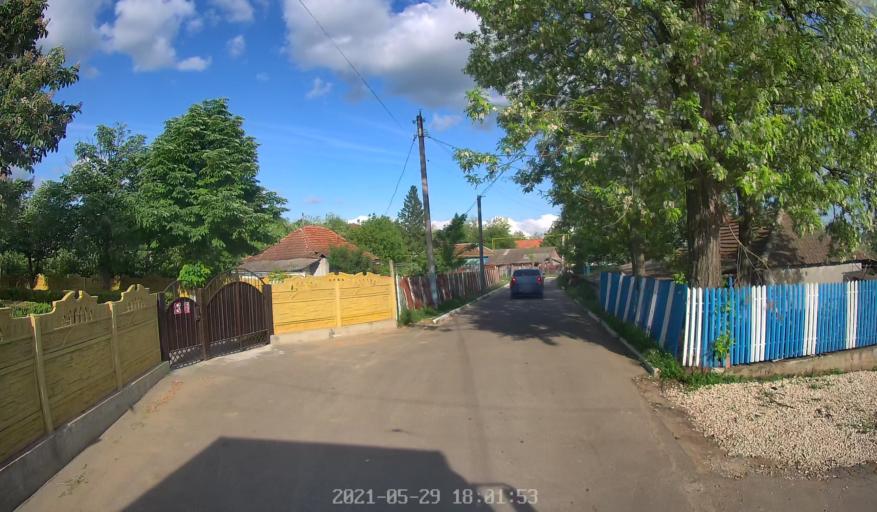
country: MD
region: Laloveni
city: Ialoveni
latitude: 46.8365
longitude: 28.8501
